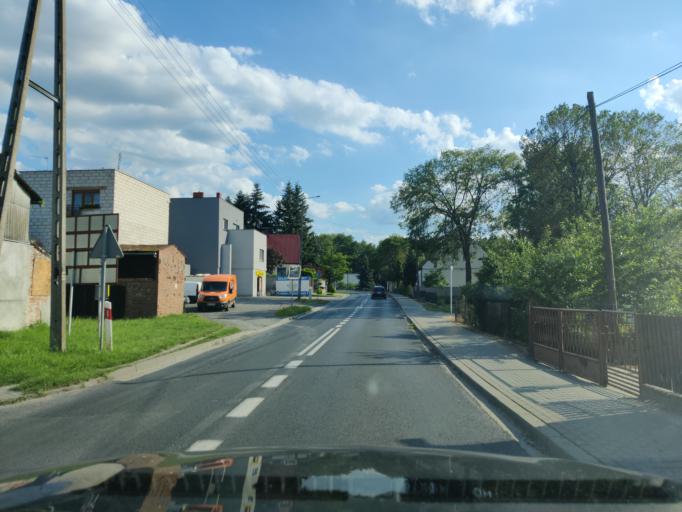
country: PL
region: Greater Poland Voivodeship
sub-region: Powiat wolsztynski
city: Wolsztyn
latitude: 52.1281
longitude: 16.1246
